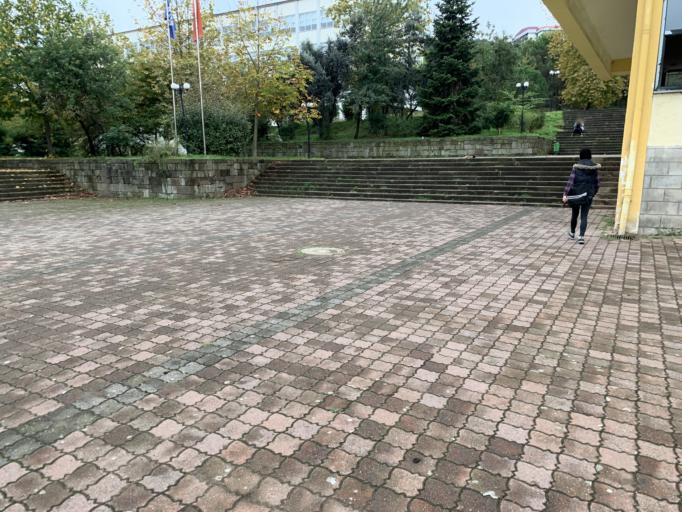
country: TR
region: Trabzon
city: Trabzon
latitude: 40.9961
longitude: 39.7727
